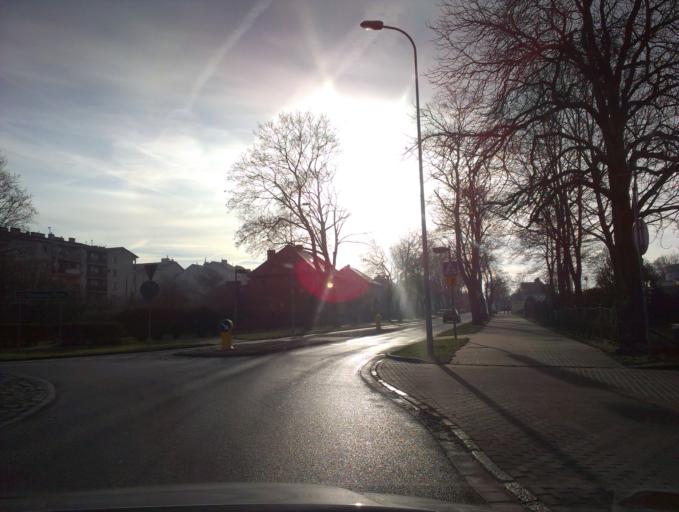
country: PL
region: West Pomeranian Voivodeship
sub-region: Powiat szczecinecki
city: Szczecinek
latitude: 53.6981
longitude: 16.6984
